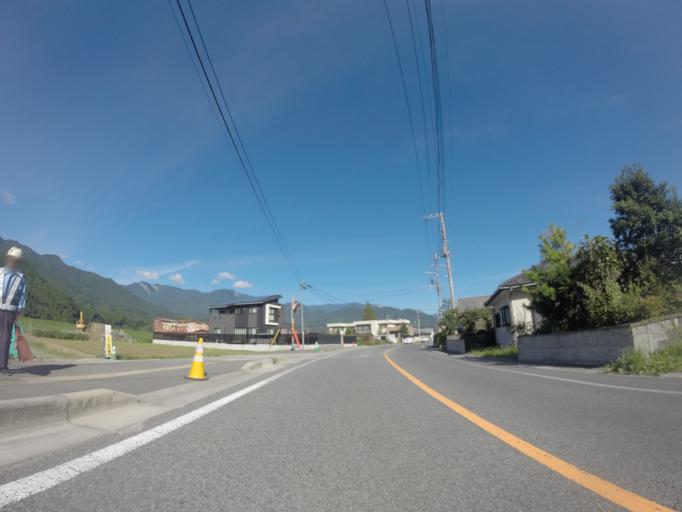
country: JP
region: Shizuoka
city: Fujinomiya
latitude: 35.2751
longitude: 138.4688
